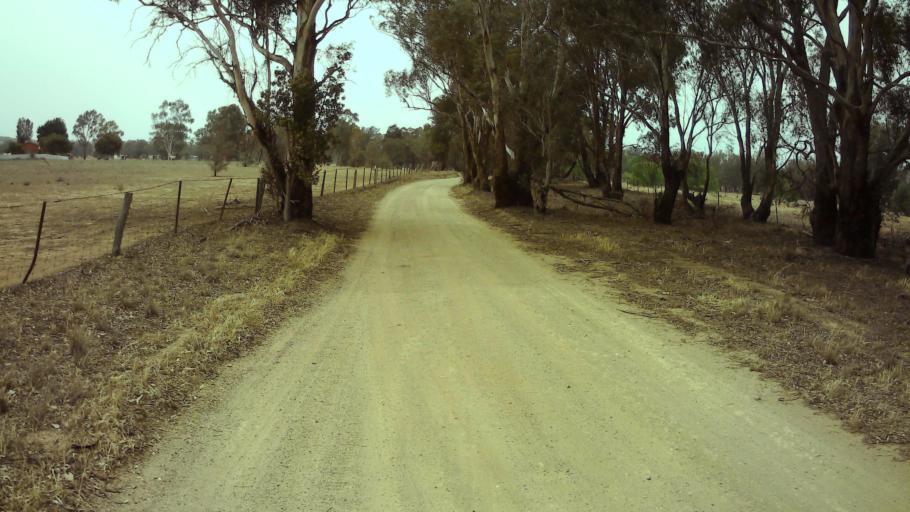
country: AU
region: New South Wales
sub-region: Weddin
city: Grenfell
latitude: -33.9044
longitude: 148.1394
